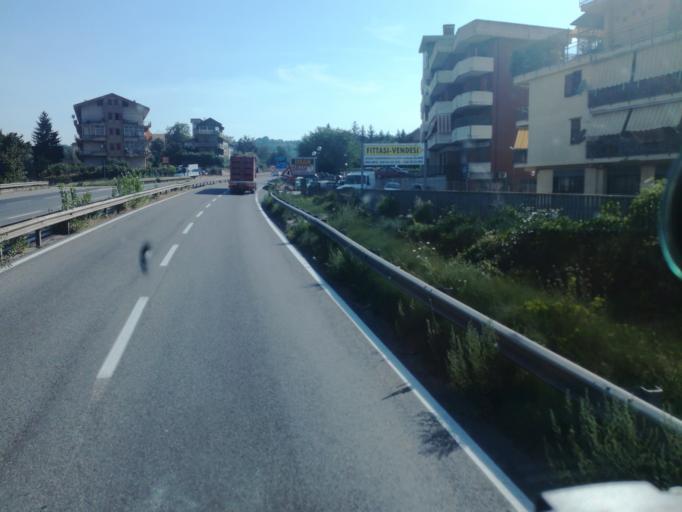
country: IT
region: Campania
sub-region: Provincia di Avellino
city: Atripalda
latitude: 40.9161
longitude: 14.8251
